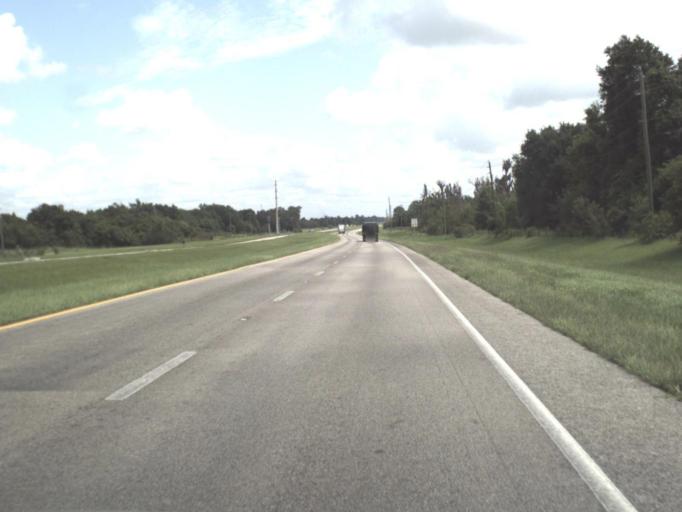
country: US
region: Florida
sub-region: DeSoto County
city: Arcadia
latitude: 27.3097
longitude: -81.8186
